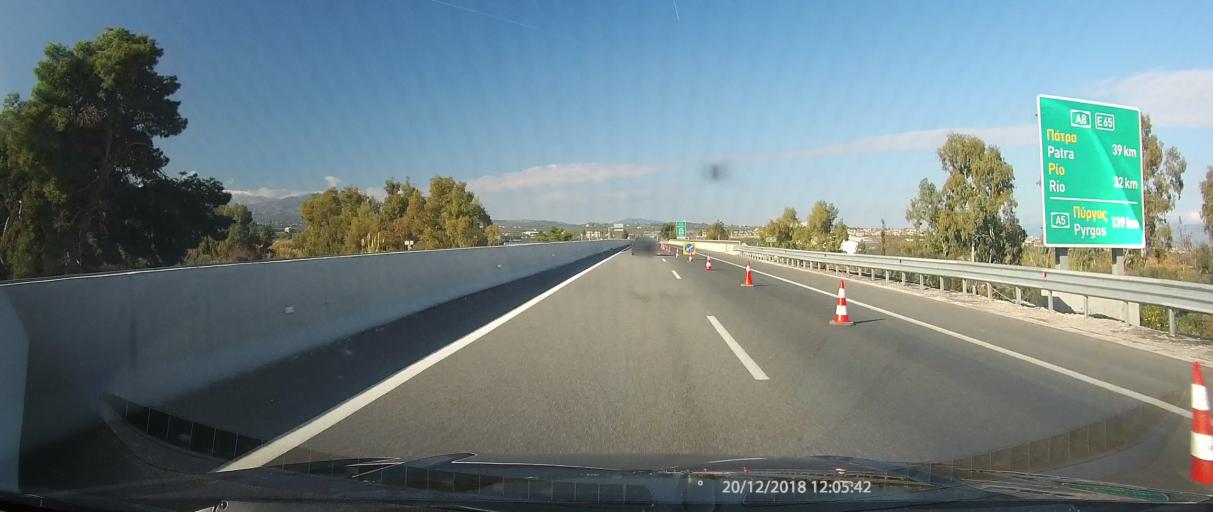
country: GR
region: West Greece
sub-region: Nomos Achaias
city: Temeni
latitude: 38.2260
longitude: 22.0935
